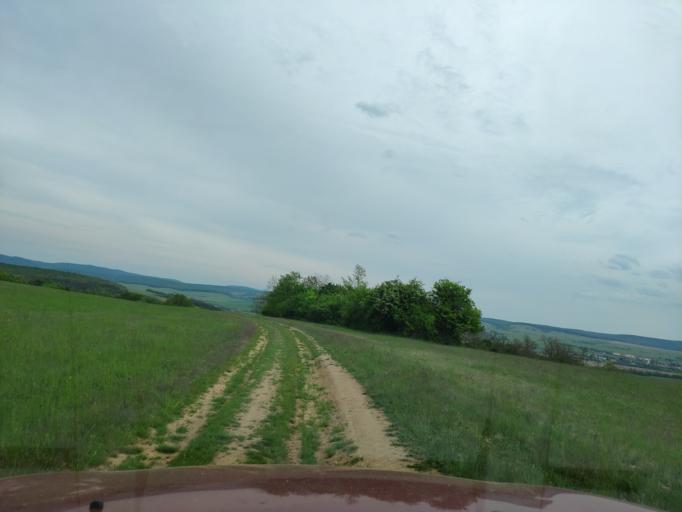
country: HU
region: Borsod-Abauj-Zemplen
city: Putnok
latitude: 48.4912
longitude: 20.3250
